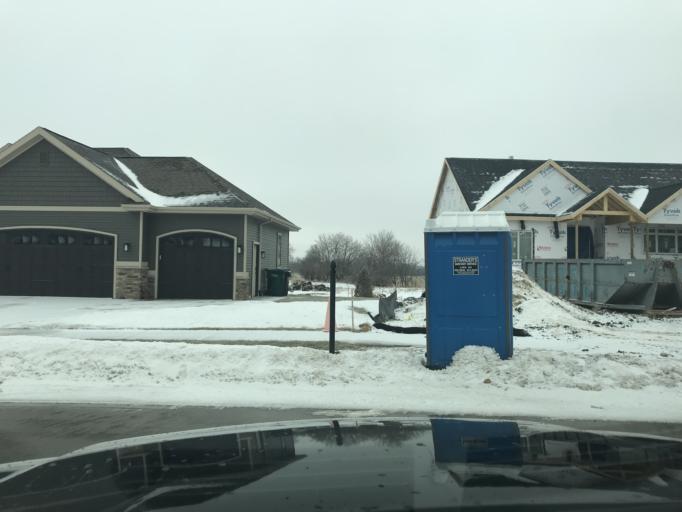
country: US
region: Wisconsin
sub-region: Dane County
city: Cottage Grove
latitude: 43.0942
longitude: -89.2237
